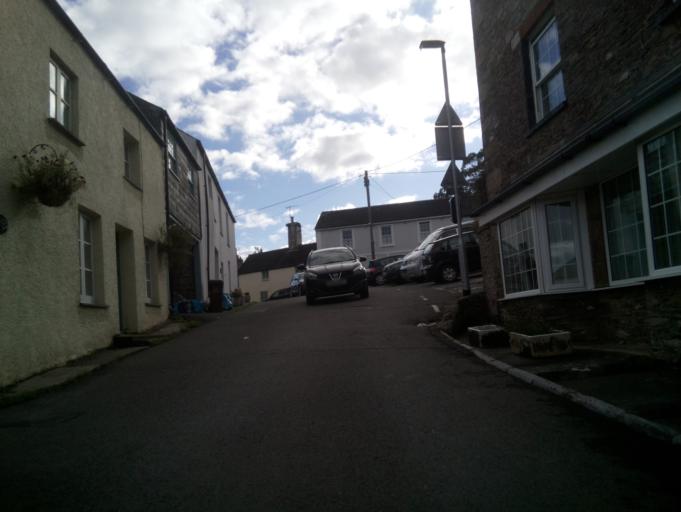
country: GB
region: England
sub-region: Devon
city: Ivybridge
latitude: 50.3618
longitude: -3.9167
